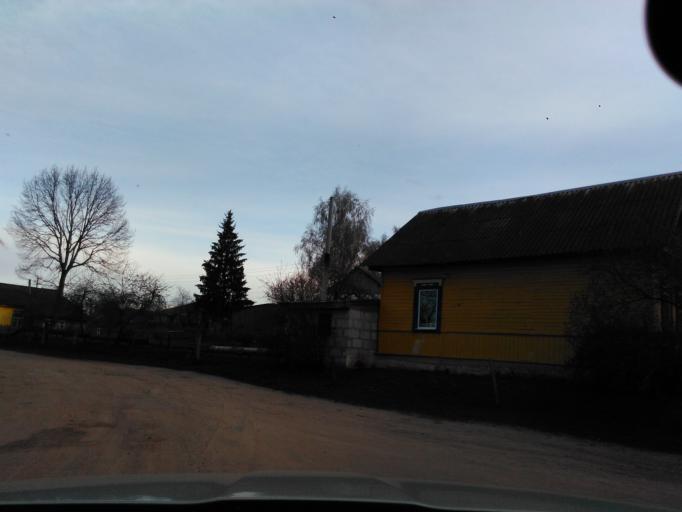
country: BY
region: Vitebsk
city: Chashniki
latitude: 54.8606
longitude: 29.1664
